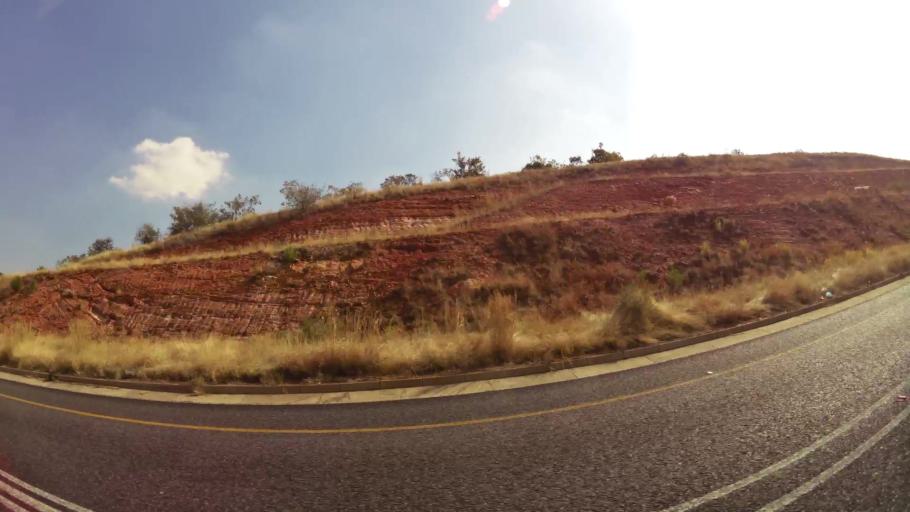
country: ZA
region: North-West
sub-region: Bojanala Platinum District Municipality
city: Rustenburg
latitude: -25.5895
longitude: 27.1276
